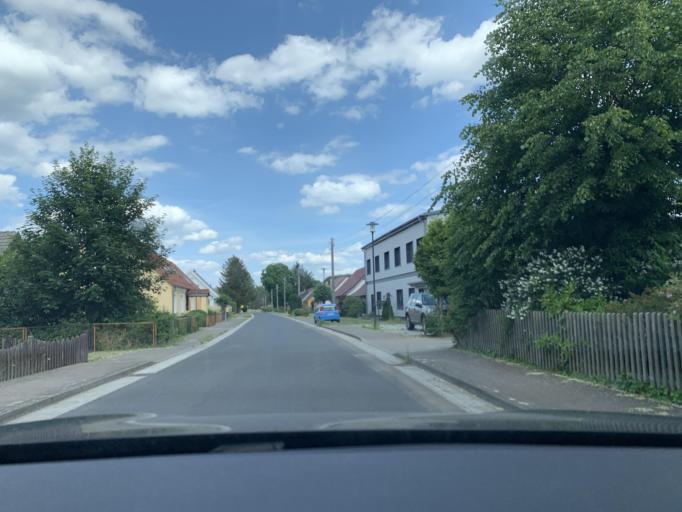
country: DE
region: Brandenburg
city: Rheinsberg
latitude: 53.1839
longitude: 12.8409
